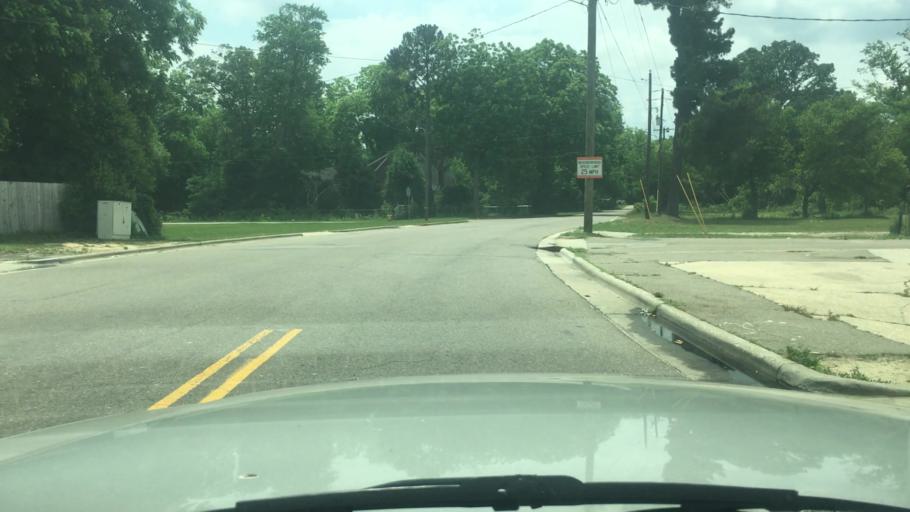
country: US
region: North Carolina
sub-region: Cumberland County
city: Fort Bragg
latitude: 35.0930
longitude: -78.9556
